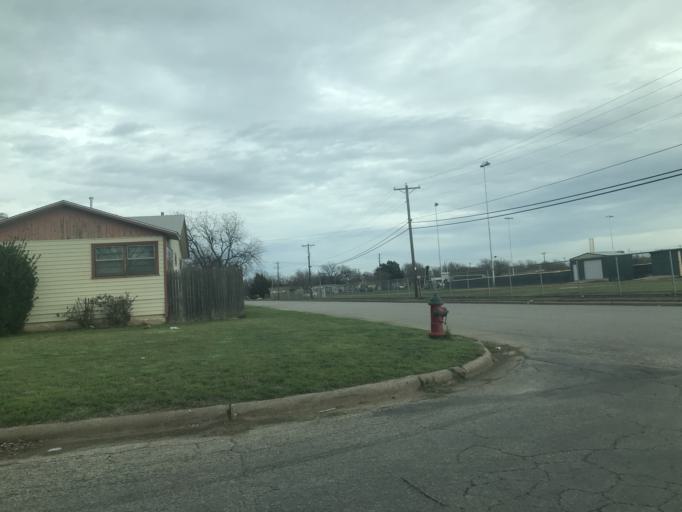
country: US
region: Texas
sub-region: Taylor County
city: Abilene
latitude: 32.4591
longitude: -99.7558
